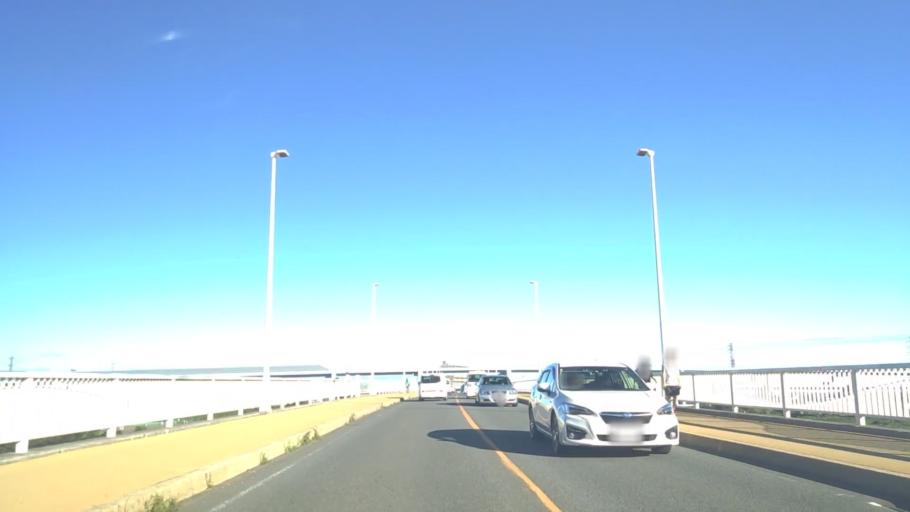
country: JP
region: Kanagawa
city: Chigasaki
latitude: 35.3745
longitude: 139.3713
